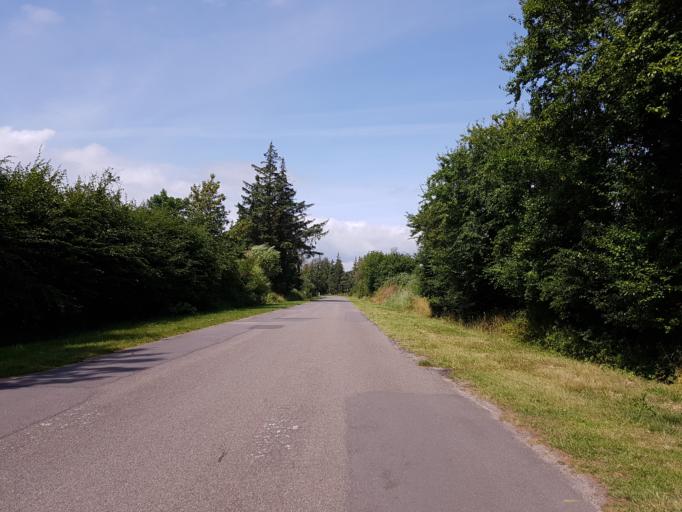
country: DK
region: Zealand
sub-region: Guldborgsund Kommune
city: Nykobing Falster
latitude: 54.5998
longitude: 11.9626
